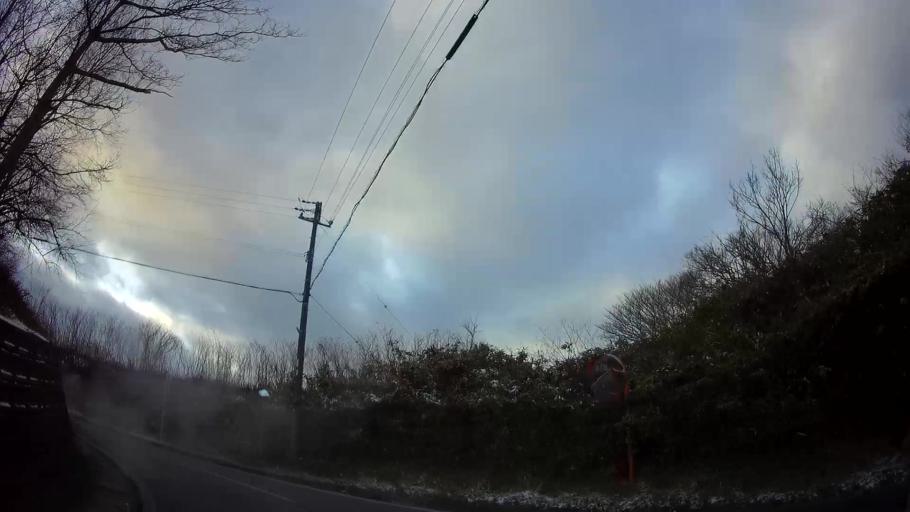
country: JP
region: Hokkaido
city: Nanae
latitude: 42.0274
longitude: 140.8323
